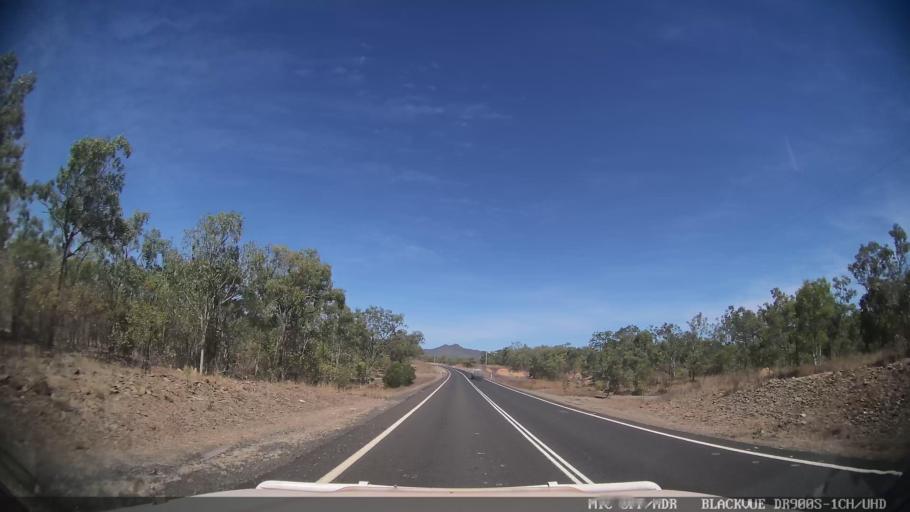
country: AU
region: Queensland
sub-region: Cook
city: Cooktown
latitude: -15.7061
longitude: 144.6098
